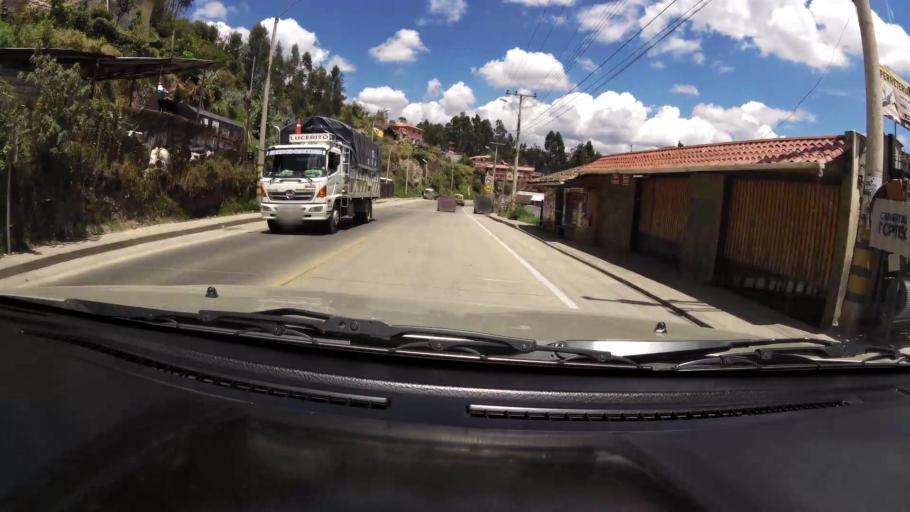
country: EC
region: Azuay
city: Cuenca
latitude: -2.9404
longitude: -79.0465
